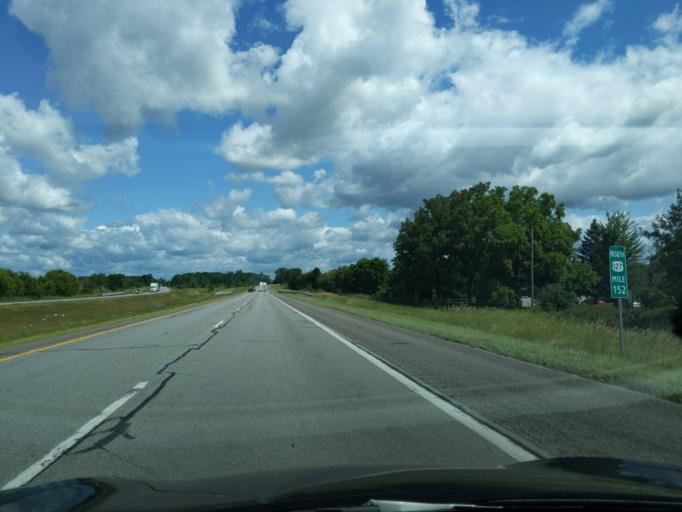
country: US
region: Michigan
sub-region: Clare County
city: Clare
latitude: 43.7420
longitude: -84.7580
